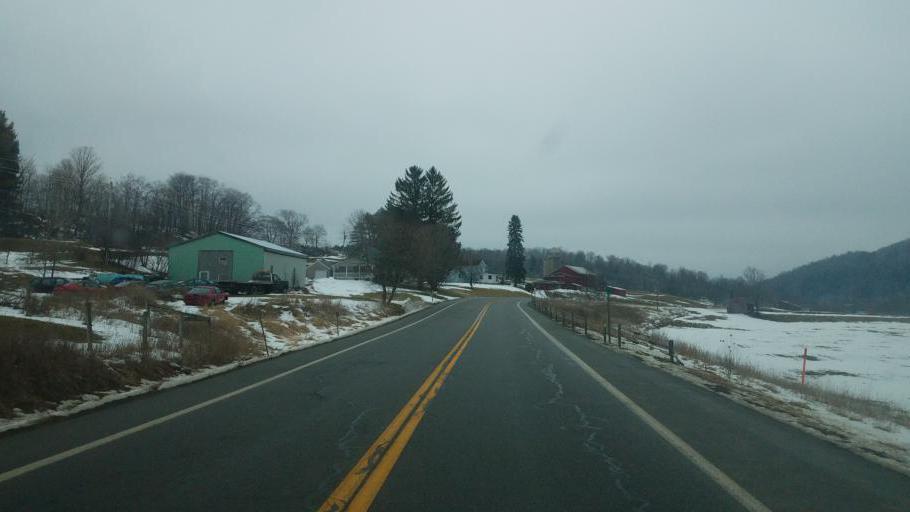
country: US
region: Pennsylvania
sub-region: Tioga County
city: Westfield
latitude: 42.0338
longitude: -77.5393
